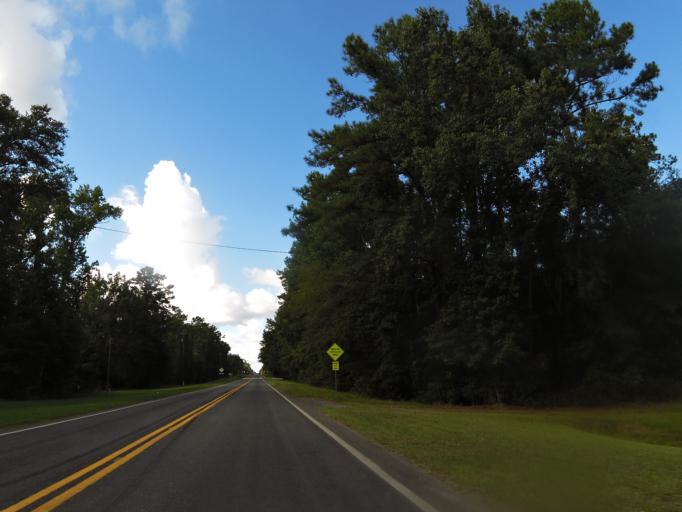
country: US
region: Georgia
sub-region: Camden County
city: Woodbine
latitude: 30.9290
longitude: -81.7157
